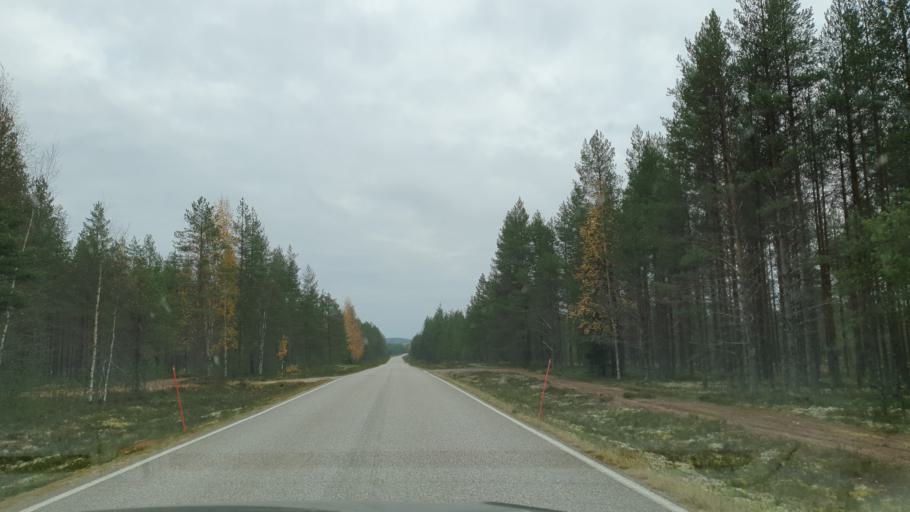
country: FI
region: Kainuu
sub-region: Kajaani
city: Paltamo
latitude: 64.6427
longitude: 27.9700
